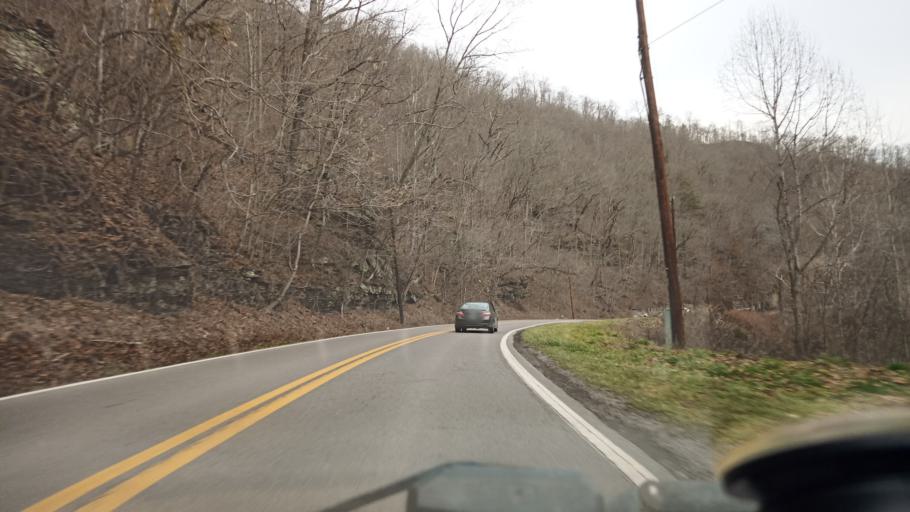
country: US
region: West Virginia
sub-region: Logan County
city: Mallory
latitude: 37.6635
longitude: -81.8599
